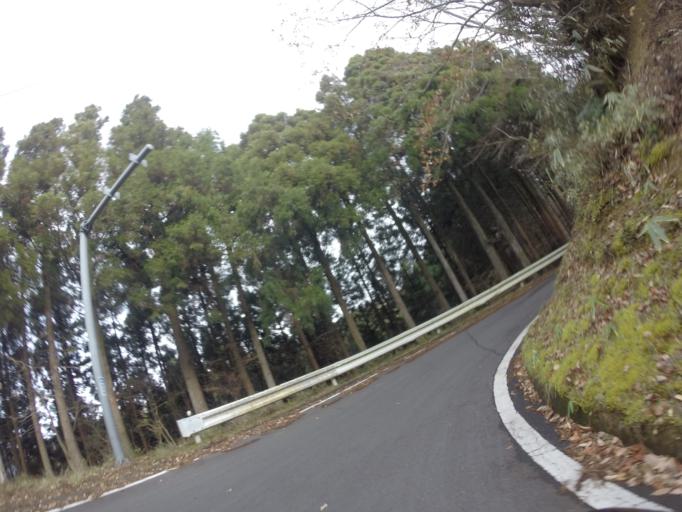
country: JP
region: Shizuoka
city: Heda
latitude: 34.8544
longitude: 138.8428
